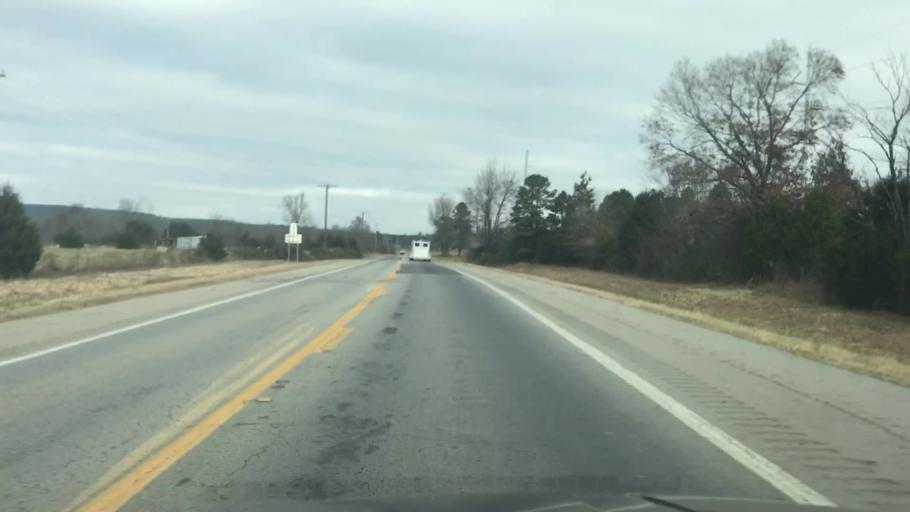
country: US
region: Arkansas
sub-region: Scott County
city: Waldron
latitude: 34.9416
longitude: -94.1025
